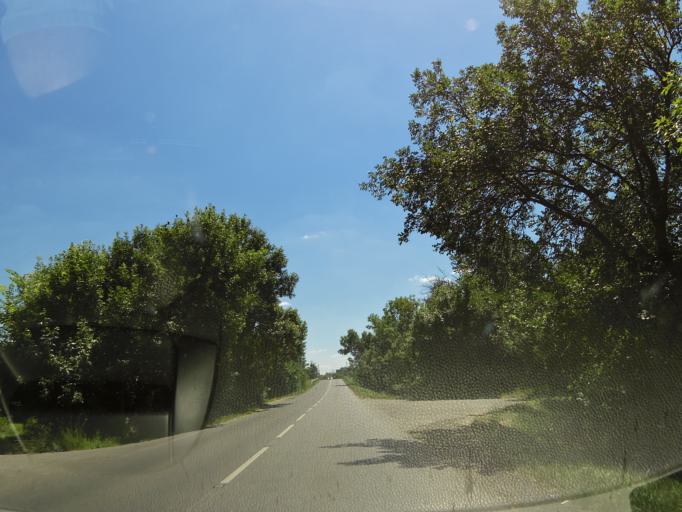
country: HU
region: Csongrad
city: Szeged
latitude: 46.2852
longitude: 20.1417
